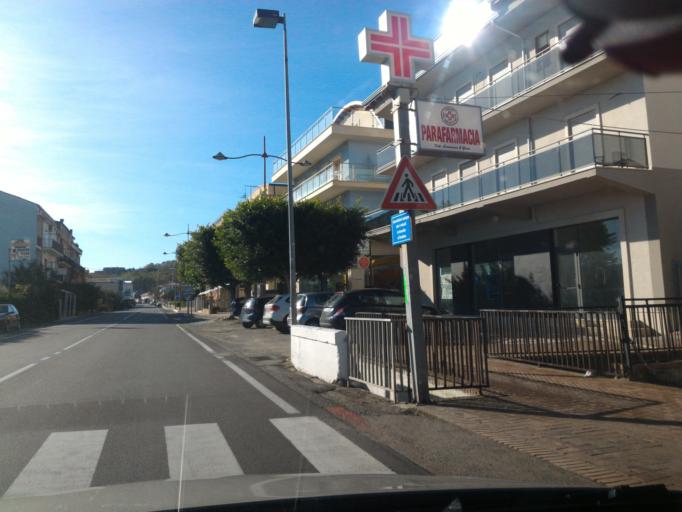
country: IT
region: Calabria
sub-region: Provincia di Crotone
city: Torre Melissa
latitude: 39.3065
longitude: 17.1081
